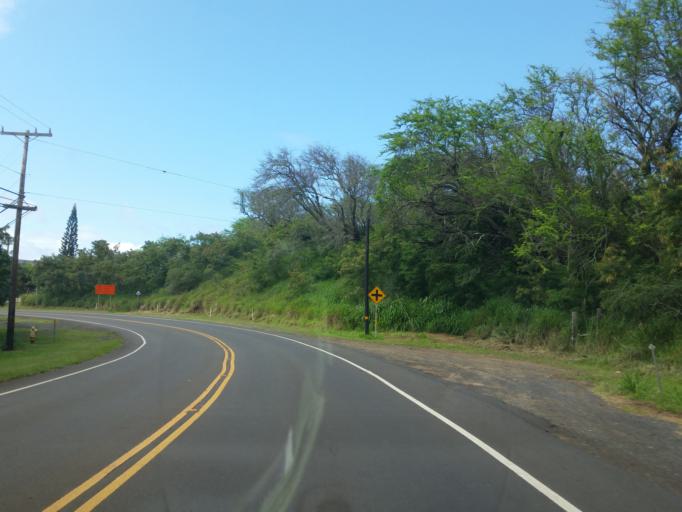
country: US
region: Hawaii
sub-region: Maui County
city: Waihee-Waiehu
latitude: 20.9422
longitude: -156.5137
